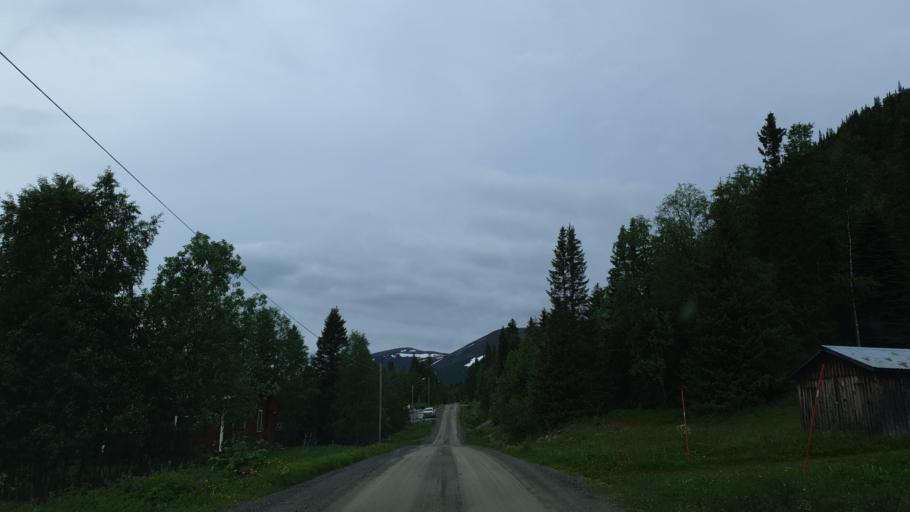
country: SE
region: Vaesterbotten
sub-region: Vilhelmina Kommun
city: Sjoberg
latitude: 65.3479
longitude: 15.8574
